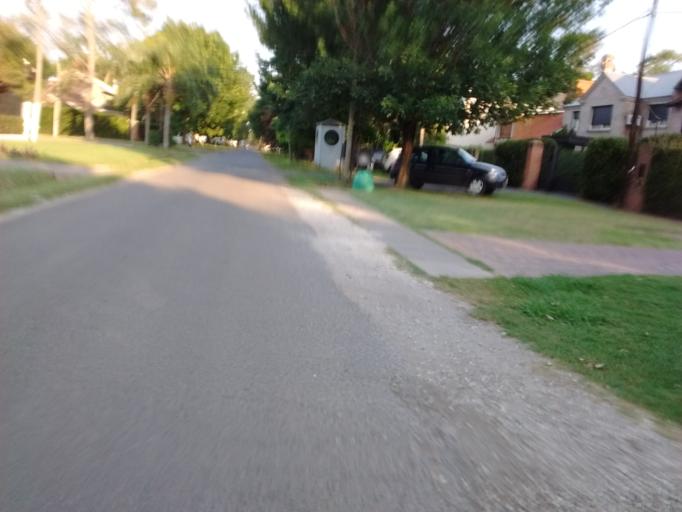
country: AR
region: Santa Fe
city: Funes
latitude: -32.9231
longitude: -60.7558
